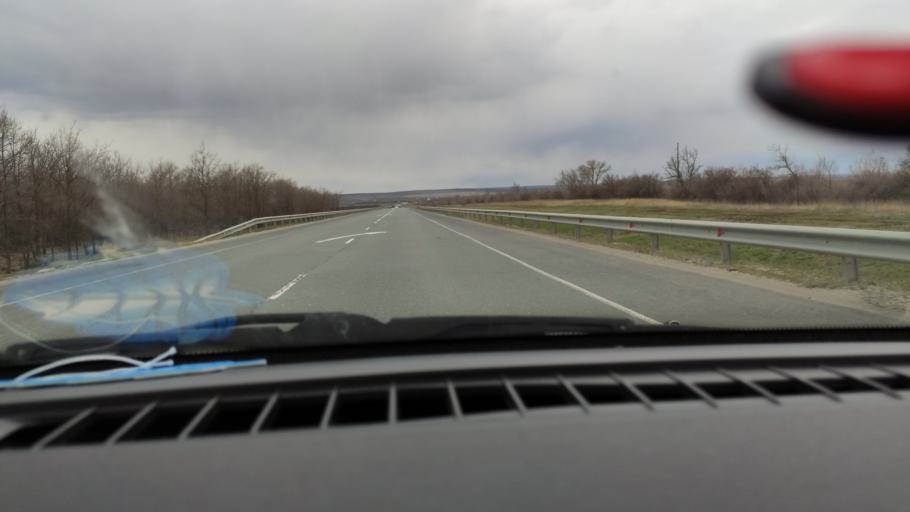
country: RU
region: Saratov
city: Yelshanka
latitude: 51.8271
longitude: 46.2670
